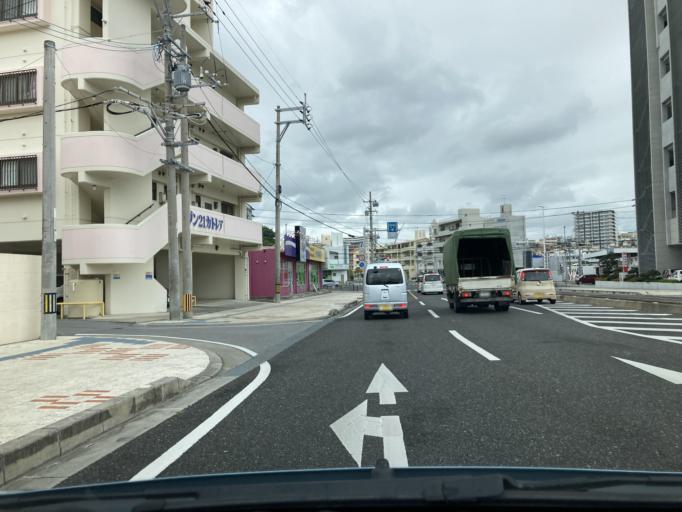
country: JP
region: Okinawa
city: Tomigusuku
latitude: 26.1964
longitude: 127.7270
